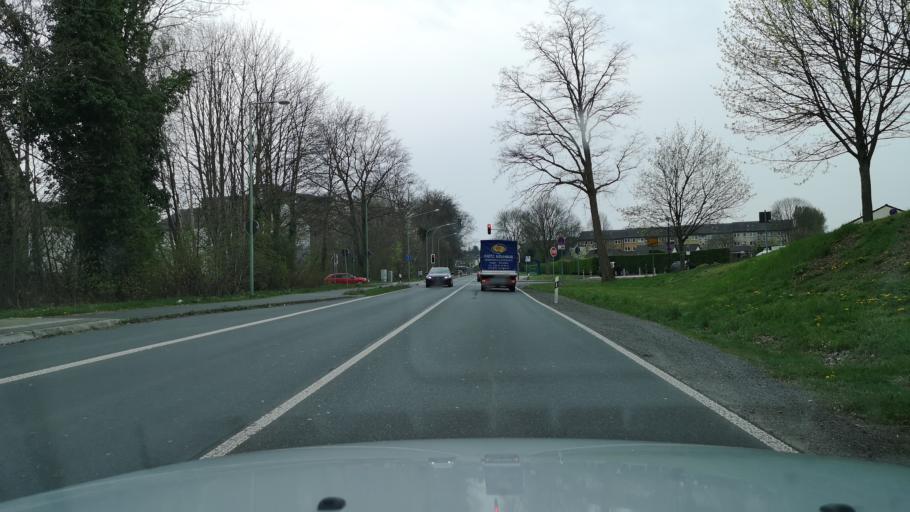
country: DE
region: North Rhine-Westphalia
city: Herdecke
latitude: 51.4014
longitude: 7.4711
